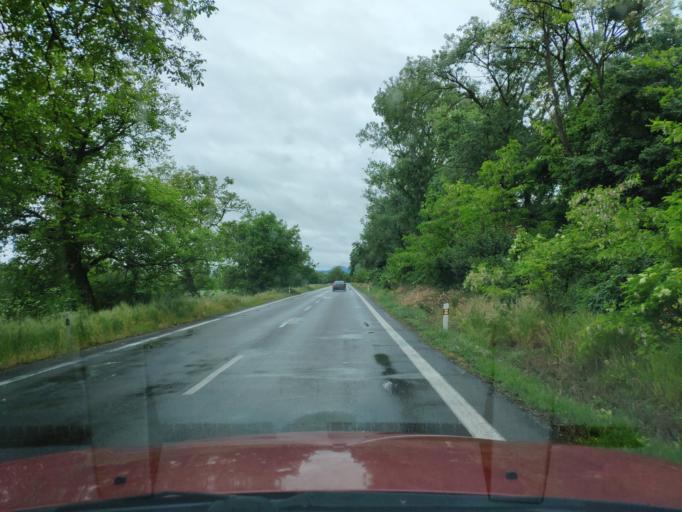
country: HU
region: Borsod-Abauj-Zemplen
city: Karcsa
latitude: 48.3899
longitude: 21.7840
